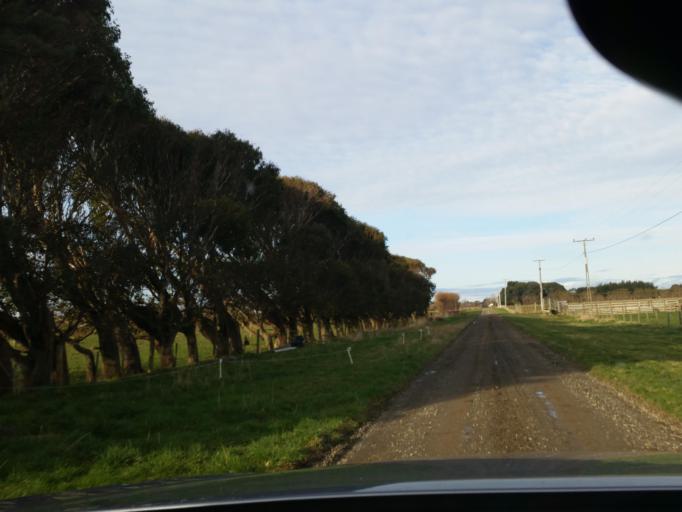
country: NZ
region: Southland
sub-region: Invercargill City
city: Invercargill
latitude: -46.3217
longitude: 168.3014
